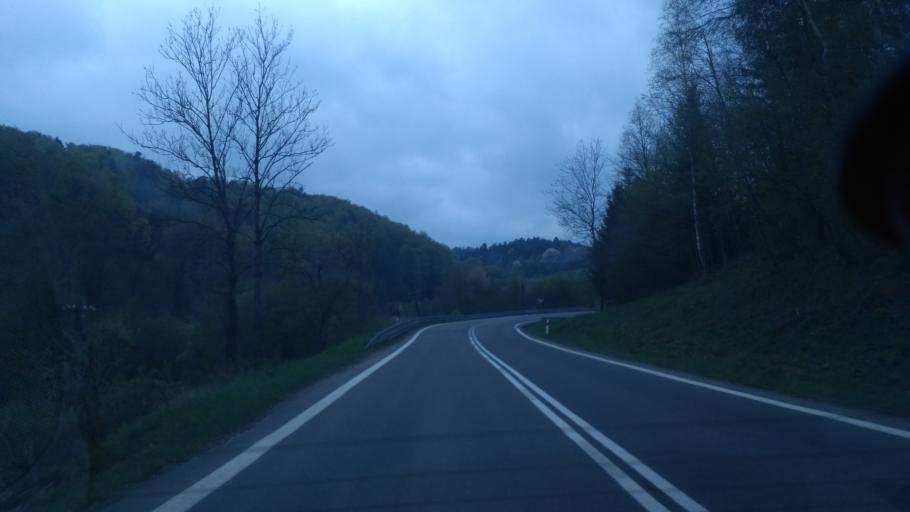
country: PL
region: Subcarpathian Voivodeship
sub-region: Powiat sanocki
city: Zagorz
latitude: 49.5403
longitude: 22.3027
